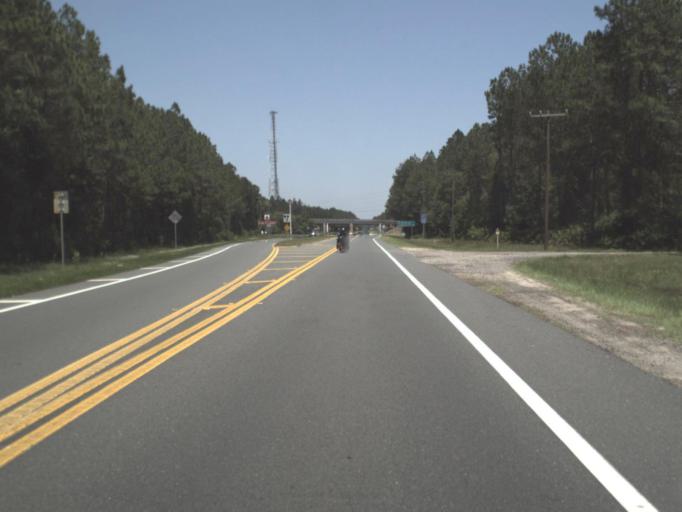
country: US
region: Florida
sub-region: Baker County
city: Macclenny
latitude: 30.2369
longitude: -82.3093
